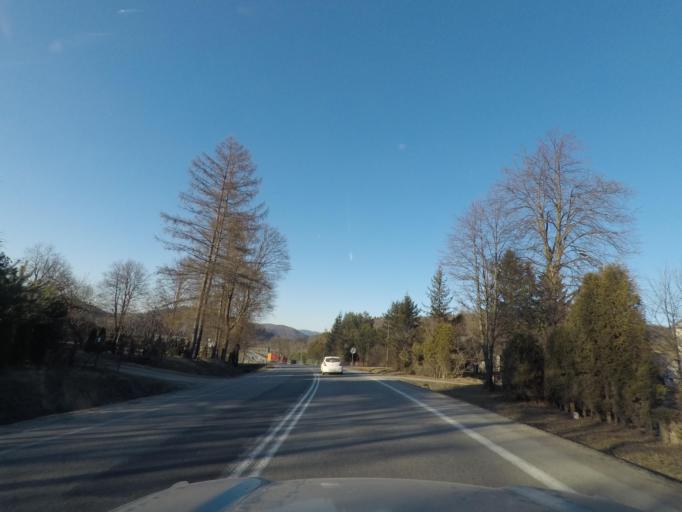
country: PL
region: Subcarpathian Voivodeship
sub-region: Powiat krosnienski
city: Jasliska
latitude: 49.4364
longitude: 21.6905
